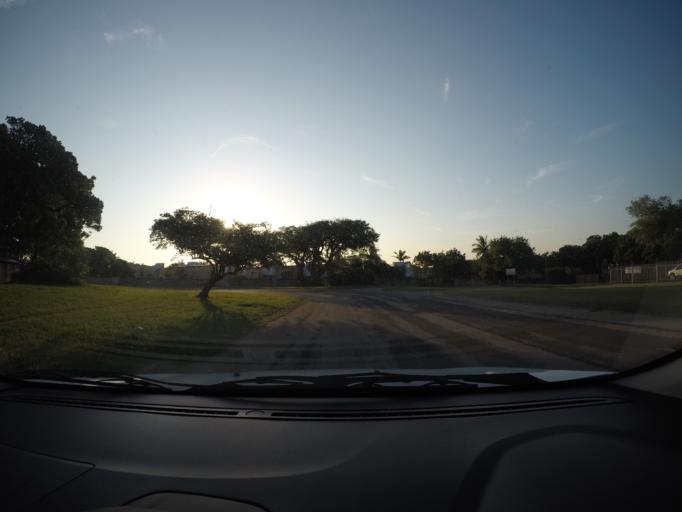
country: ZA
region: KwaZulu-Natal
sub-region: uThungulu District Municipality
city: Richards Bay
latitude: -28.7802
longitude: 32.1014
